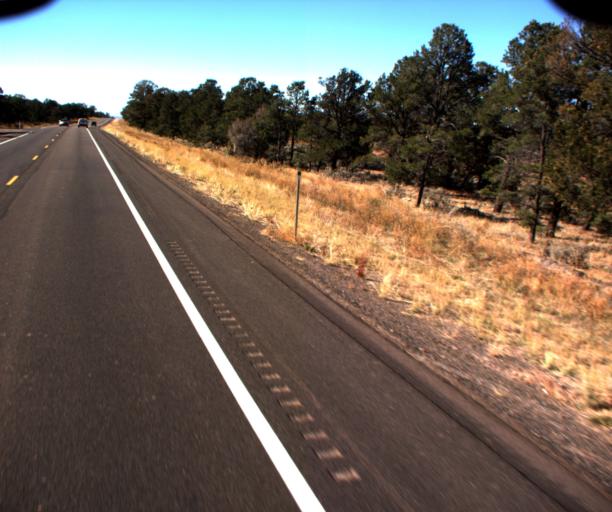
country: US
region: Arizona
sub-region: Apache County
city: Saint Michaels
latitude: 35.7040
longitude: -109.3044
